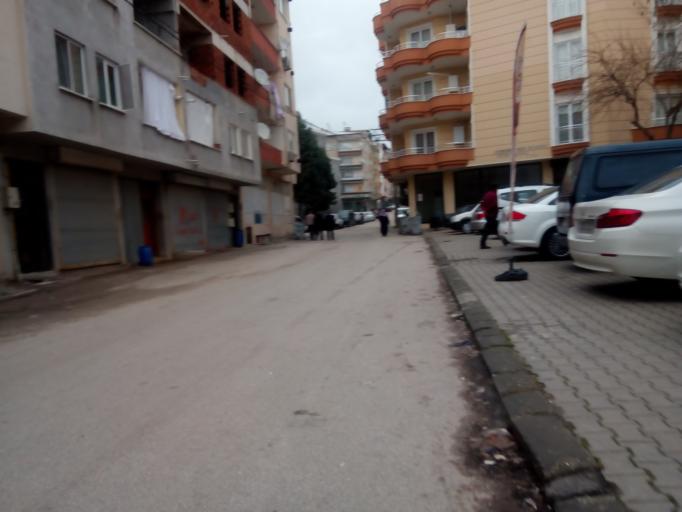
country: TR
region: Bursa
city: Niluefer
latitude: 40.2558
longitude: 28.9617
